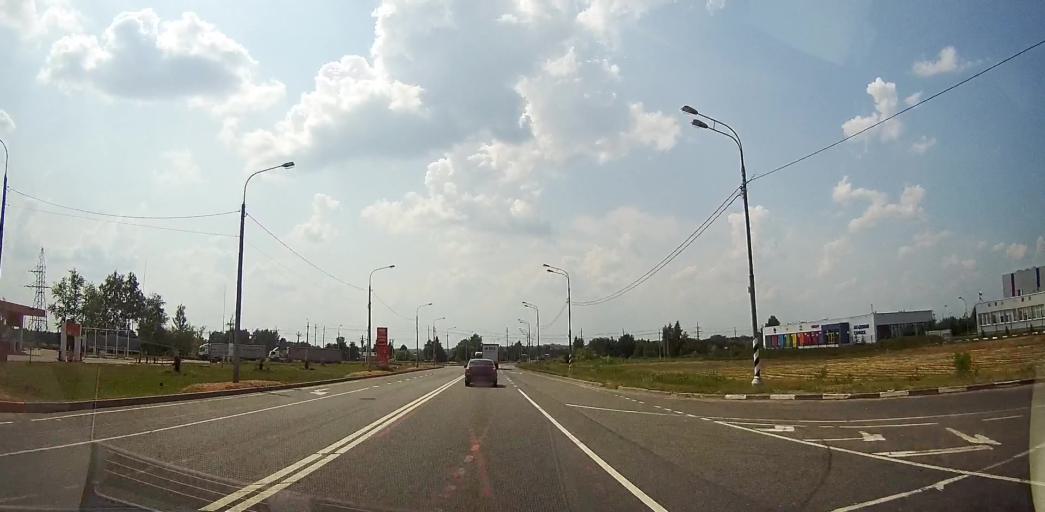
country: RU
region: Moskovskaya
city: Malino
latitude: 55.1158
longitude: 38.1972
